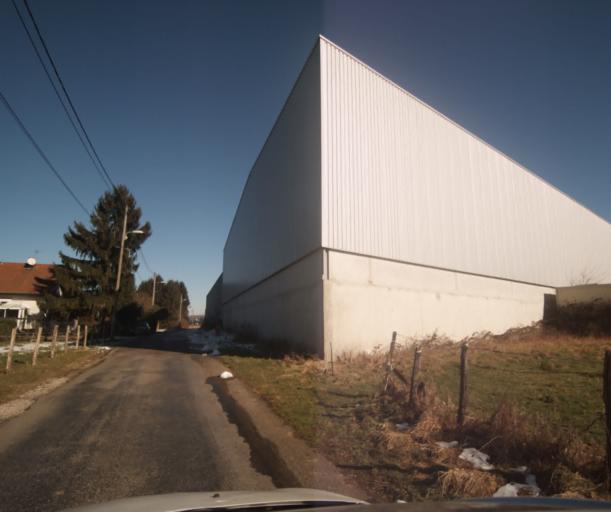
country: FR
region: Franche-Comte
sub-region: Departement du Doubs
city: Thise
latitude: 47.2698
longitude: 6.0541
